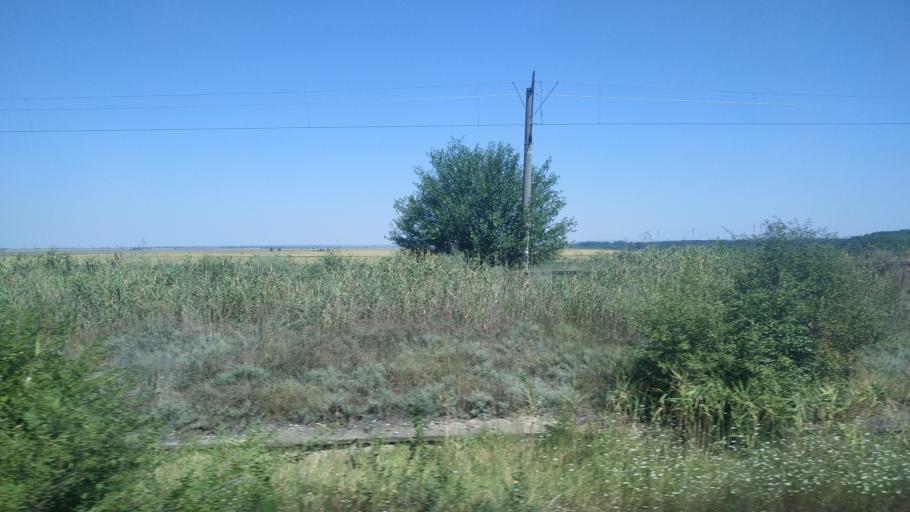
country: RO
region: Constanta
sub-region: Oras Cernavoda
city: Cernavoda
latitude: 44.3447
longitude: 27.9984
